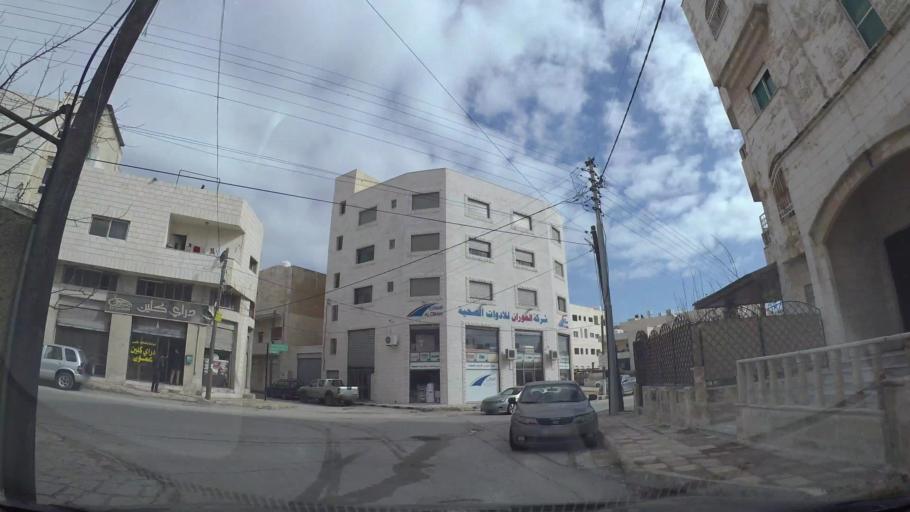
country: JO
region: Amman
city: Wadi as Sir
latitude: 31.9486
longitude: 35.8411
